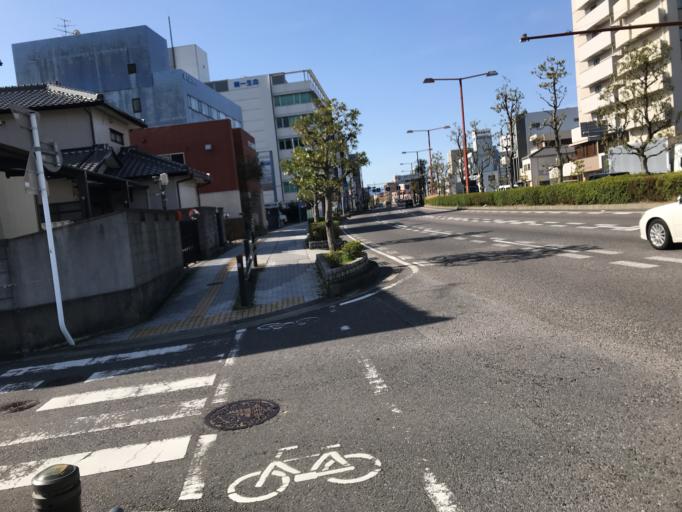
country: JP
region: Mie
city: Tsu-shi
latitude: 34.7309
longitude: 136.5130
